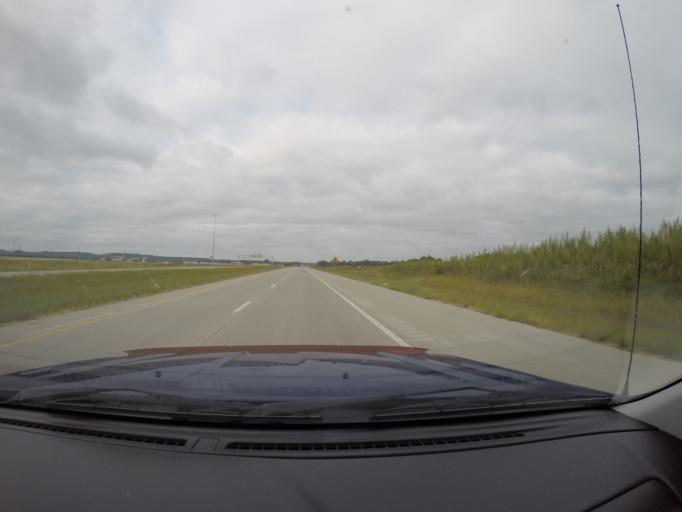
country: US
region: Kansas
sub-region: Riley County
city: Ogden
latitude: 39.1309
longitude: -96.6717
